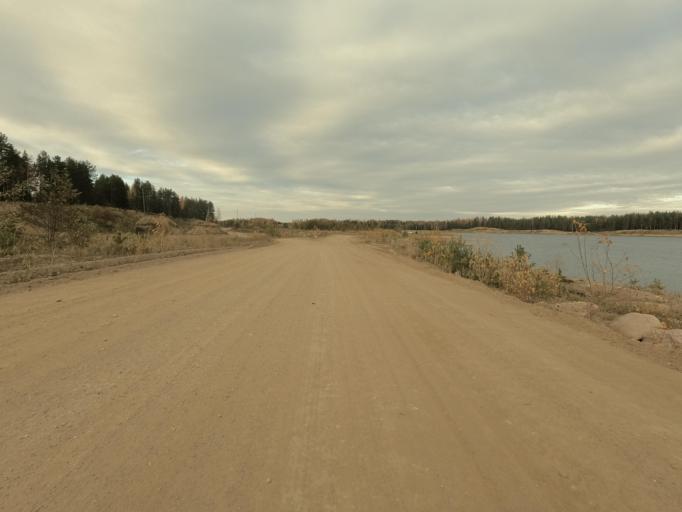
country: RU
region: Leningrad
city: Priladozhskiy
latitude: 59.7064
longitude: 31.3643
